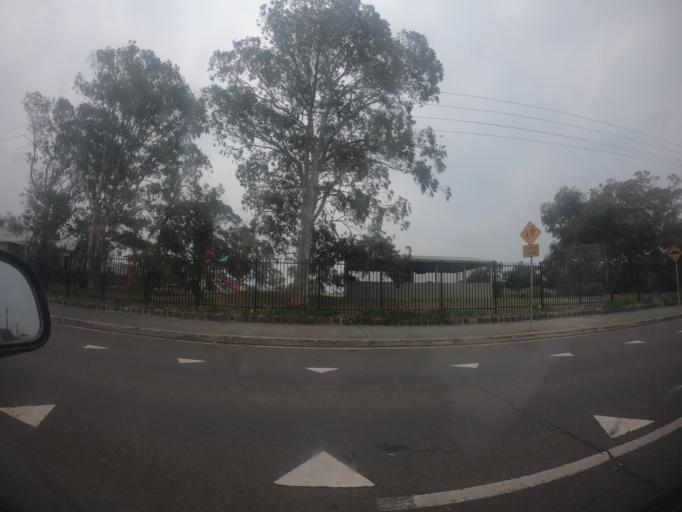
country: AU
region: New South Wales
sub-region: Shellharbour
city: Shellharbour Village
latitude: -34.5800
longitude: 150.8650
